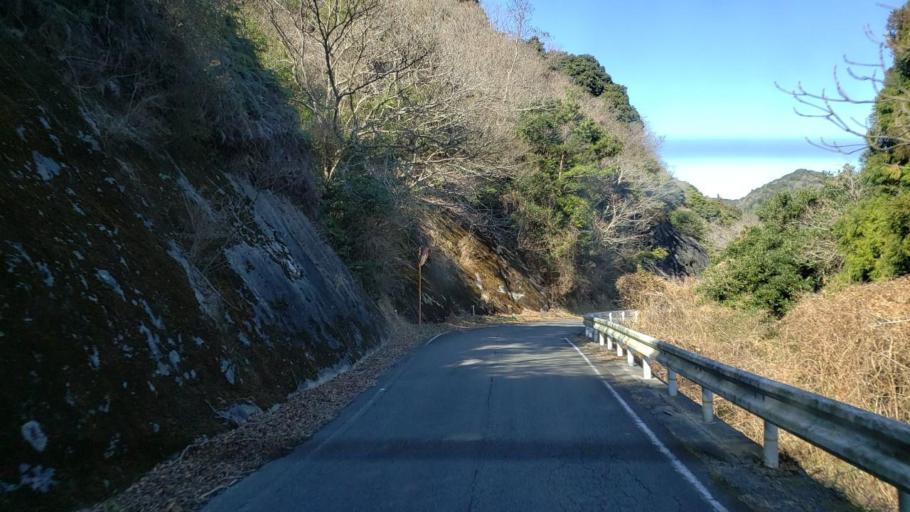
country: JP
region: Tokushima
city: Narutocho-mitsuishi
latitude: 34.2043
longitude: 134.5529
